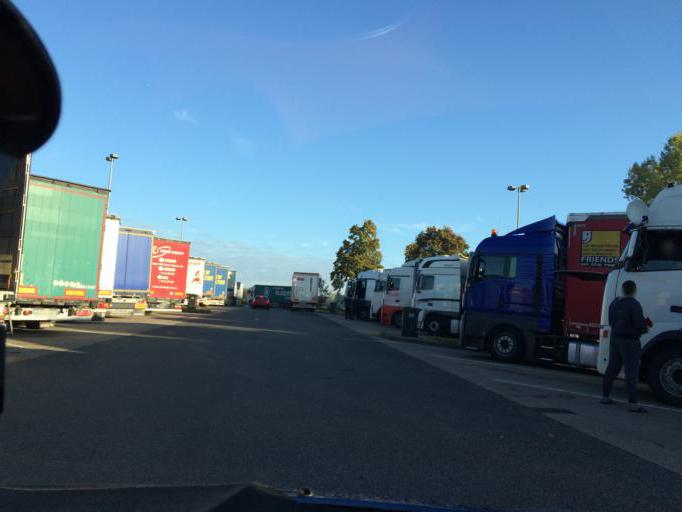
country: DE
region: North Rhine-Westphalia
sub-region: Regierungsbezirk Koln
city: Erftstadt
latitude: 50.8581
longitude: 6.8061
